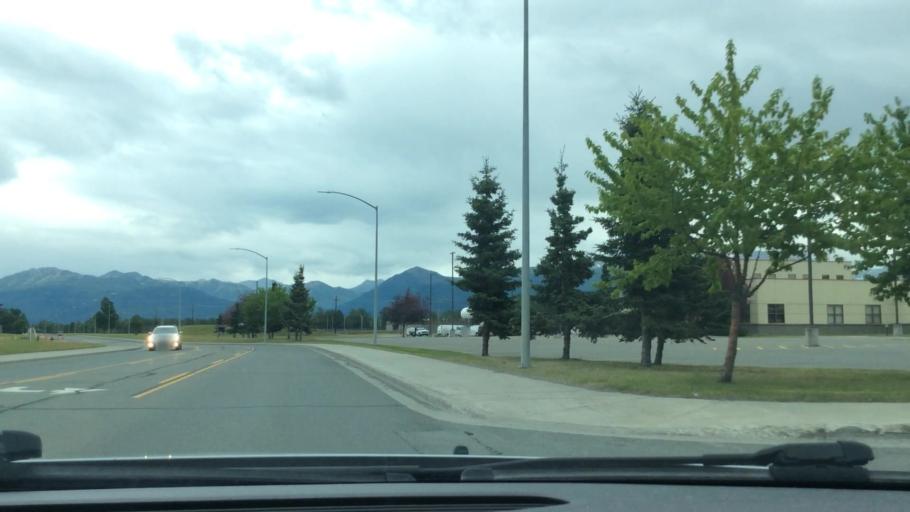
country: US
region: Alaska
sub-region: Anchorage Municipality
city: Anchorage
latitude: 61.2372
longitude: -149.8296
